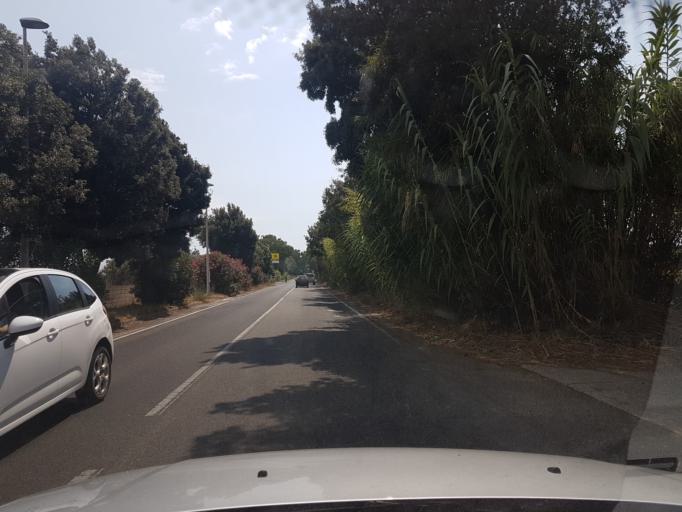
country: IT
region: Sardinia
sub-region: Provincia di Oristano
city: Donigala Fenugheddu
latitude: 39.9258
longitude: 8.5757
